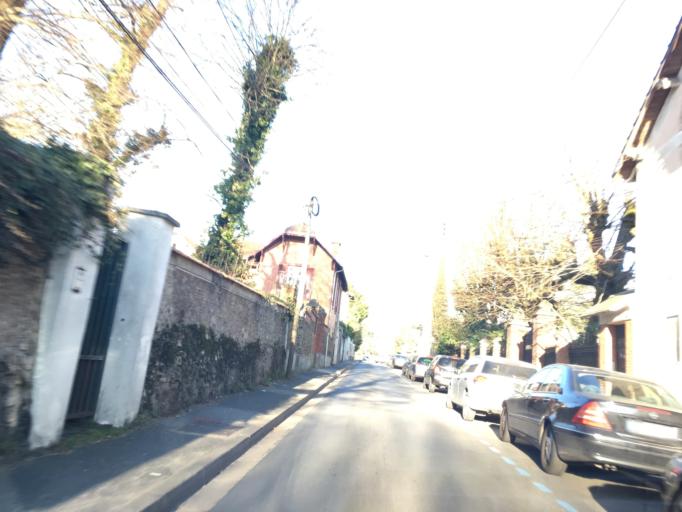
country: FR
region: Ile-de-France
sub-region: Departement de l'Essonne
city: Epinay-sous-Senart
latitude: 48.7014
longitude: 2.5094
